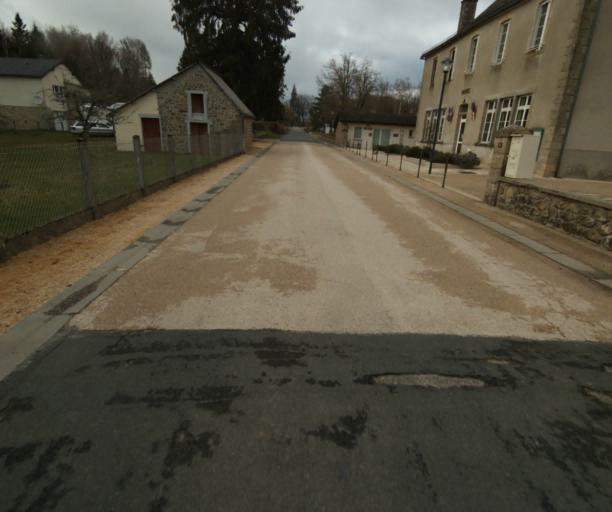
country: FR
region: Limousin
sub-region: Departement de la Correze
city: Saint-Privat
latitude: 45.2151
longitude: 2.0037
